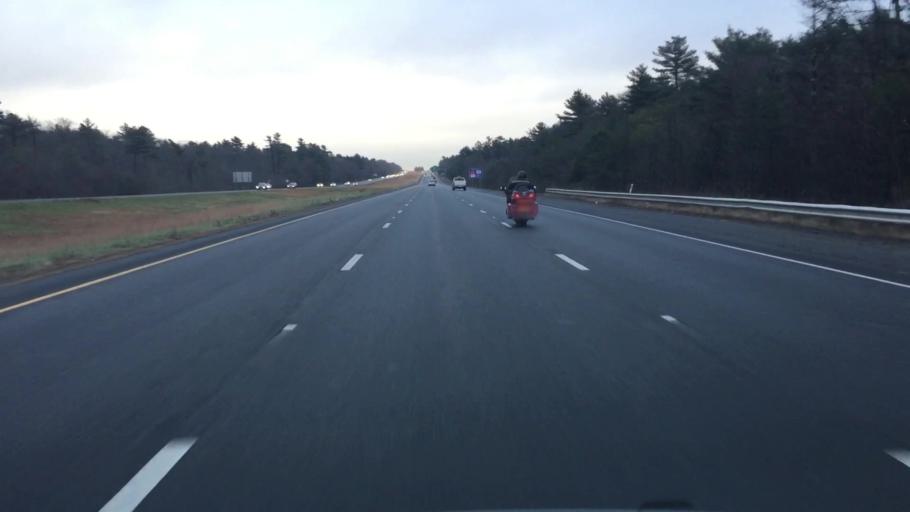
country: US
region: Massachusetts
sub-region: Bristol County
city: Raynham
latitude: 41.9607
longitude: -71.0985
